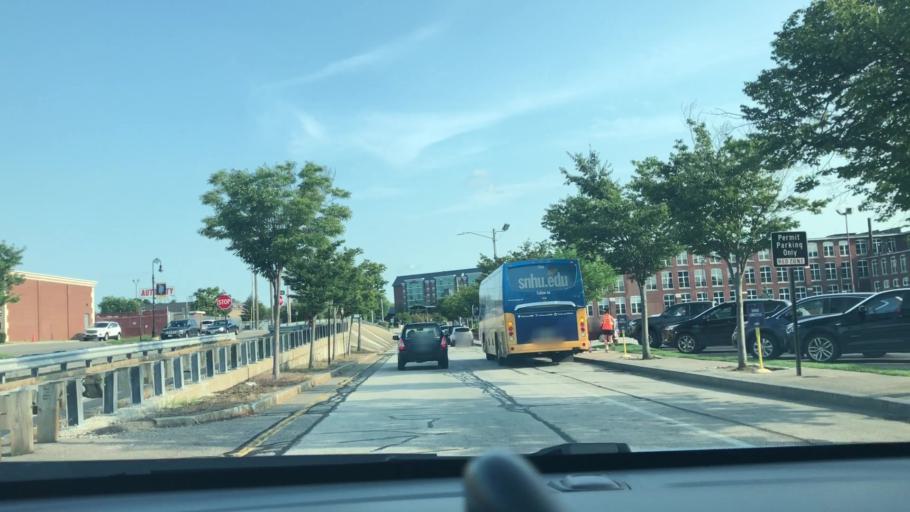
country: US
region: New Hampshire
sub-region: Hillsborough County
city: Manchester
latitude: 42.9854
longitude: -71.4675
